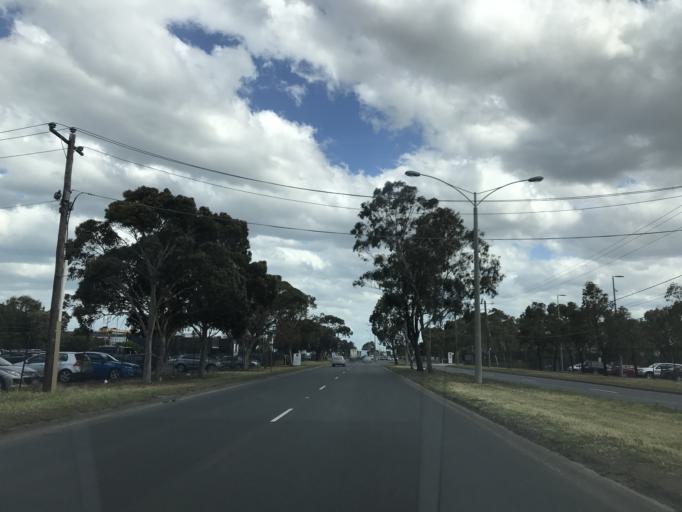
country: AU
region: Victoria
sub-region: Brimbank
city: Sunshine West
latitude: -37.8085
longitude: 144.8183
